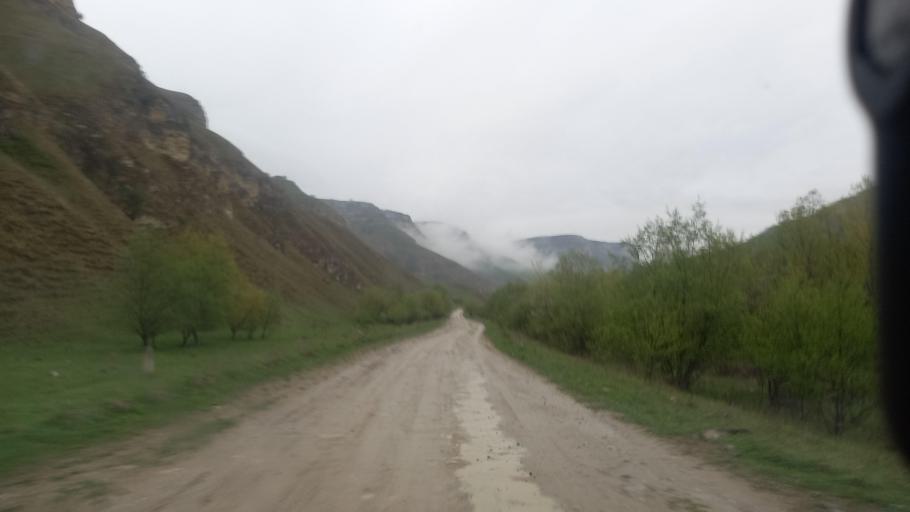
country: RU
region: Kabardino-Balkariya
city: Gundelen
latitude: 43.5984
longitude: 43.0588
